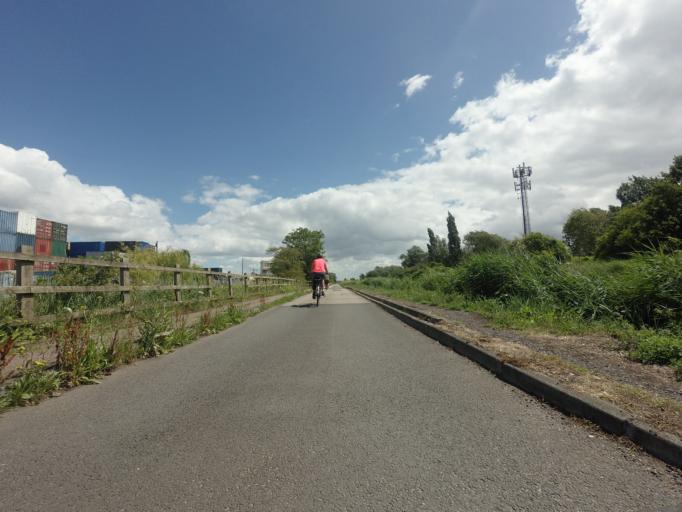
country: GB
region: England
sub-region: Kent
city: Gravesend
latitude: 51.4415
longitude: 0.3957
